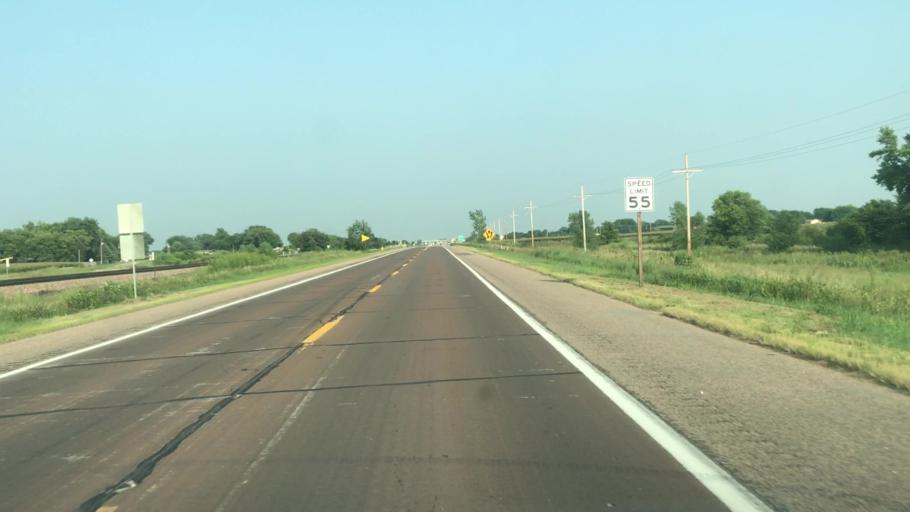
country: US
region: Nebraska
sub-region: Hall County
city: Grand Island
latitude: 40.9603
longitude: -98.4151
